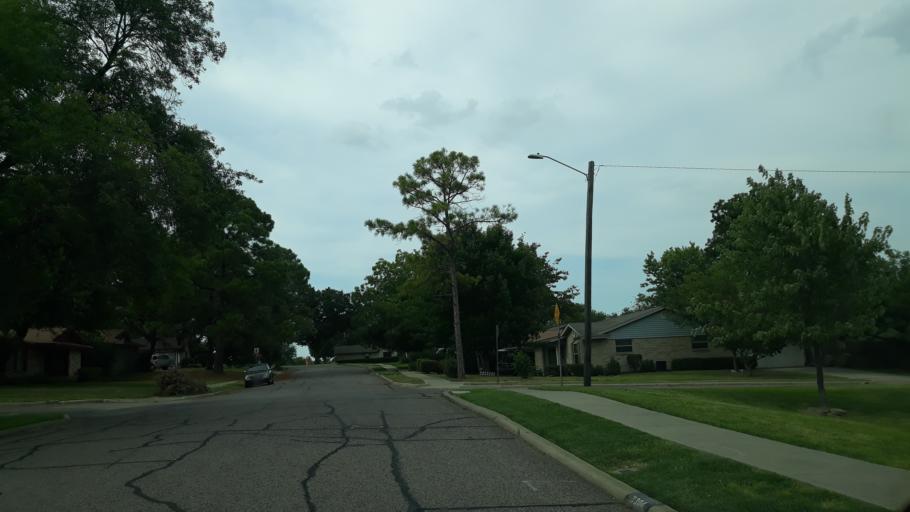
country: US
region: Texas
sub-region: Dallas County
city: Irving
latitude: 32.8512
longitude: -96.9819
